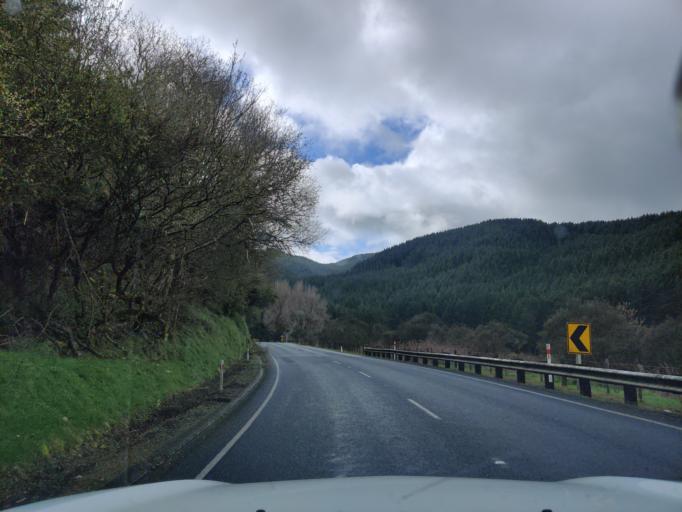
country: NZ
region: Waikato
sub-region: Otorohanga District
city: Otorohanga
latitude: -38.6478
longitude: 175.2098
